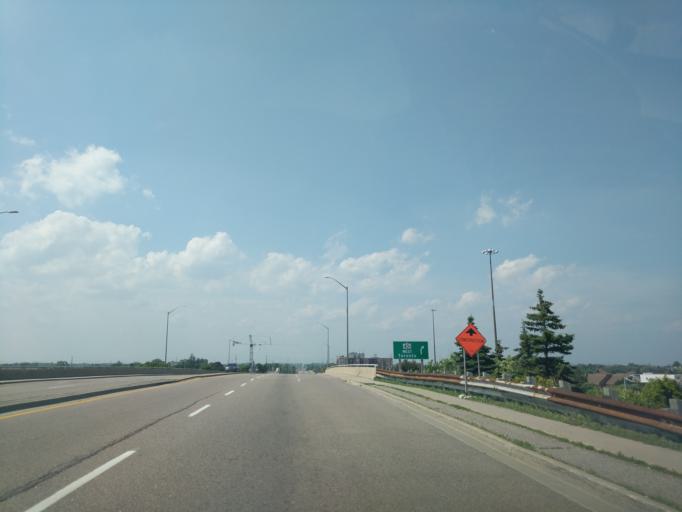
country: CA
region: Ontario
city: Pickering
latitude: 43.8157
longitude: -79.1141
